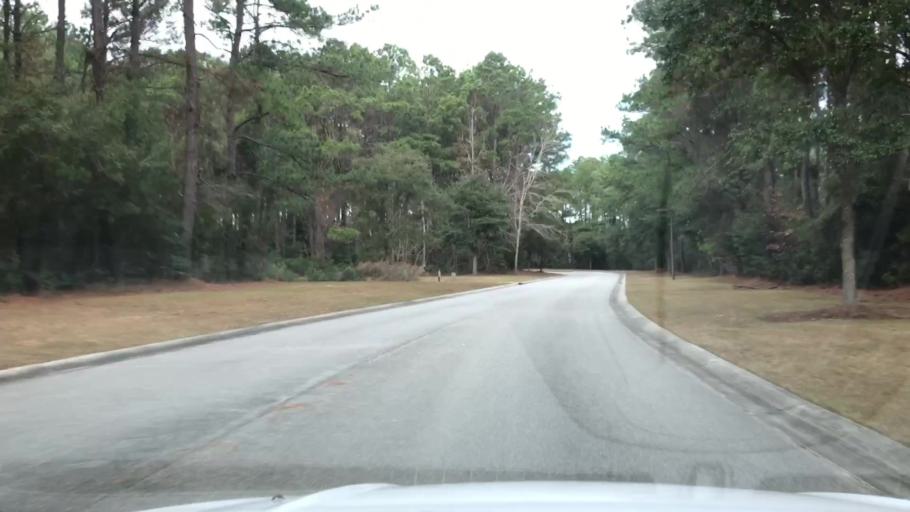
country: US
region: South Carolina
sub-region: Charleston County
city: Isle of Palms
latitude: 32.9075
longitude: -79.7217
